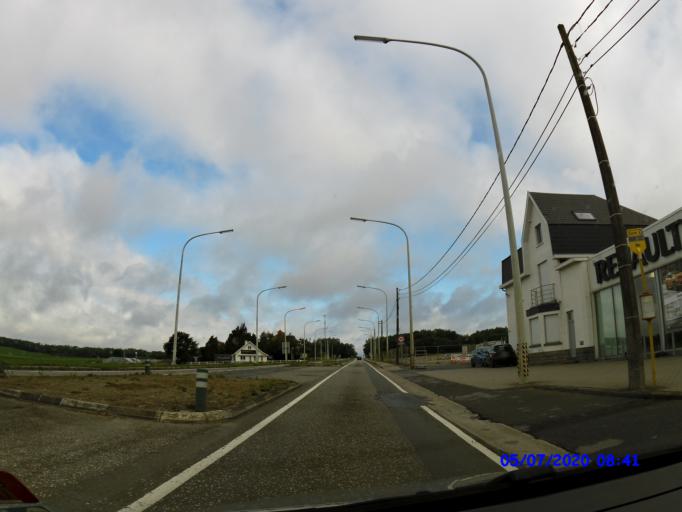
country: BE
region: Wallonia
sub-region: Province du Brabant Wallon
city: Genappe
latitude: 50.6182
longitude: 4.4434
